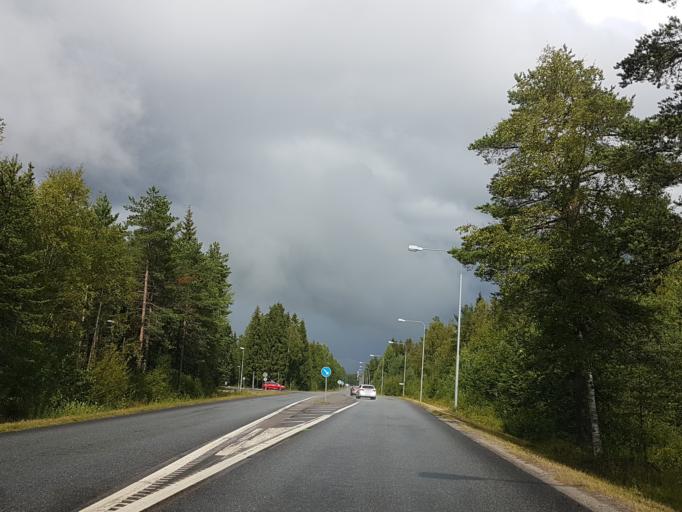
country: SE
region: Vaesterbotten
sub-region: Umea Kommun
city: Ersmark
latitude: 63.8515
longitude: 20.3436
